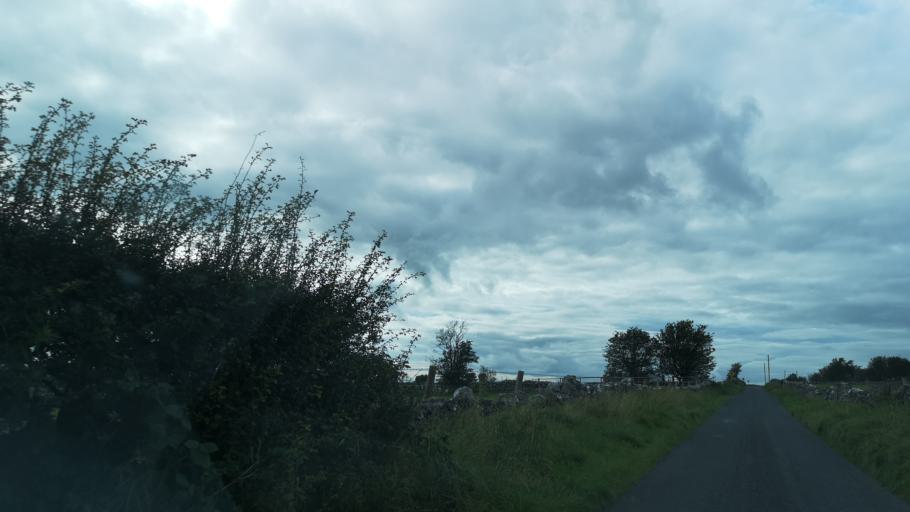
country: IE
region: Connaught
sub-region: County Galway
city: Ballinasloe
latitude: 53.3793
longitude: -8.1755
